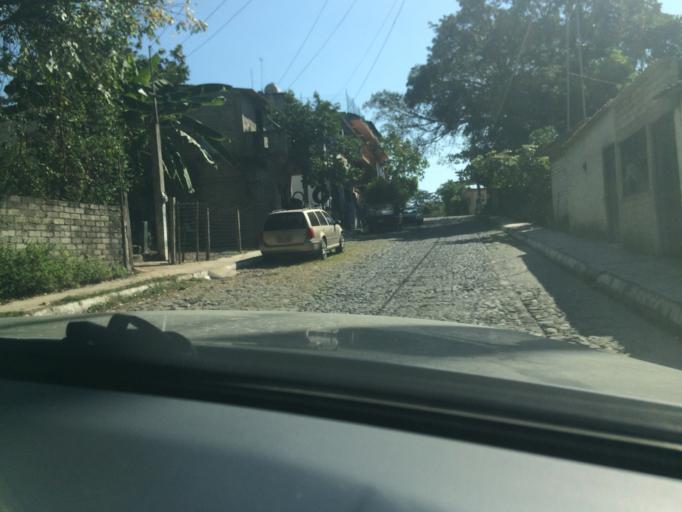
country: MX
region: Colima
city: Suchitlan
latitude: 19.3742
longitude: -103.7147
